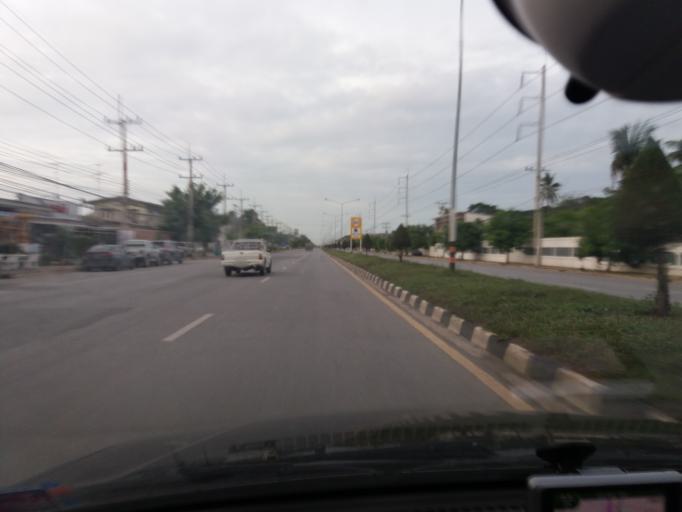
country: TH
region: Suphan Buri
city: U Thong
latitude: 14.3977
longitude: 99.8959
